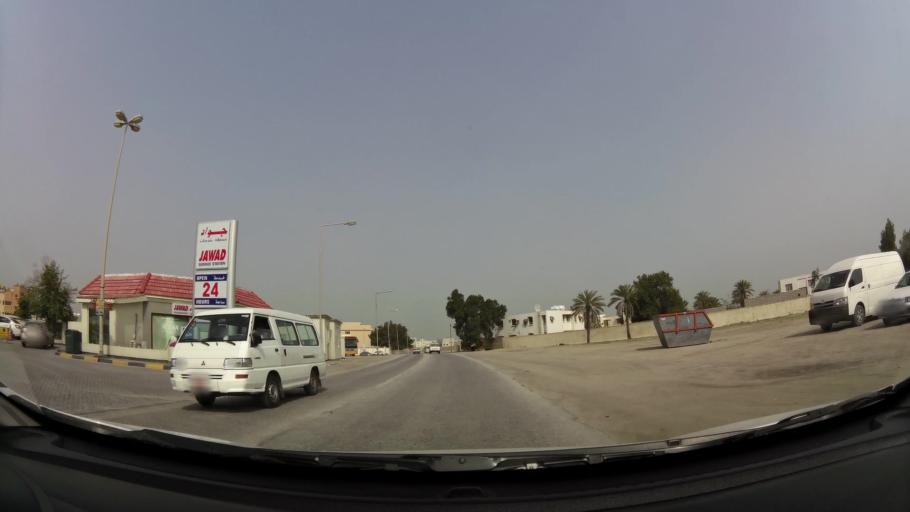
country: BH
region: Manama
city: Jidd Hafs
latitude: 26.2248
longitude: 50.5213
